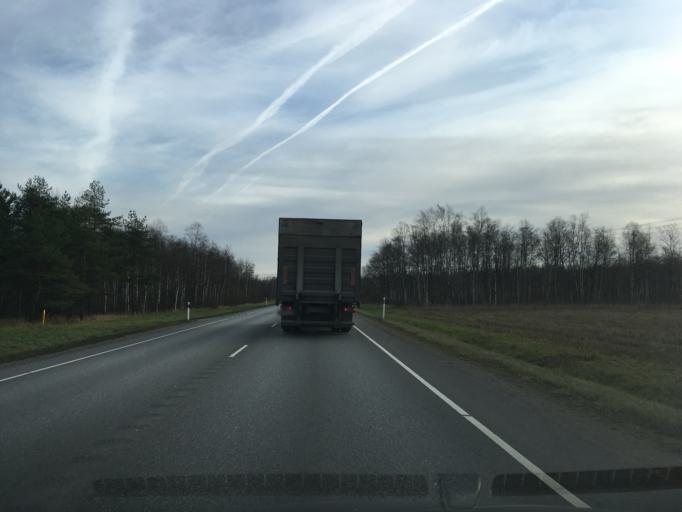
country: EE
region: Ida-Virumaa
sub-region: Kohtla-Jaerve linn
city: Kohtla-Jarve
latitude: 59.4208
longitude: 27.2510
